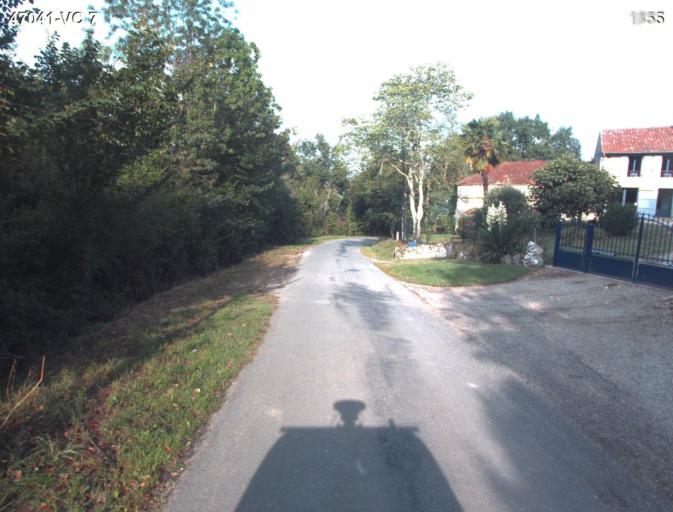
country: FR
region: Aquitaine
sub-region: Departement du Lot-et-Garonne
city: Port-Sainte-Marie
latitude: 44.1941
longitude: 0.4194
